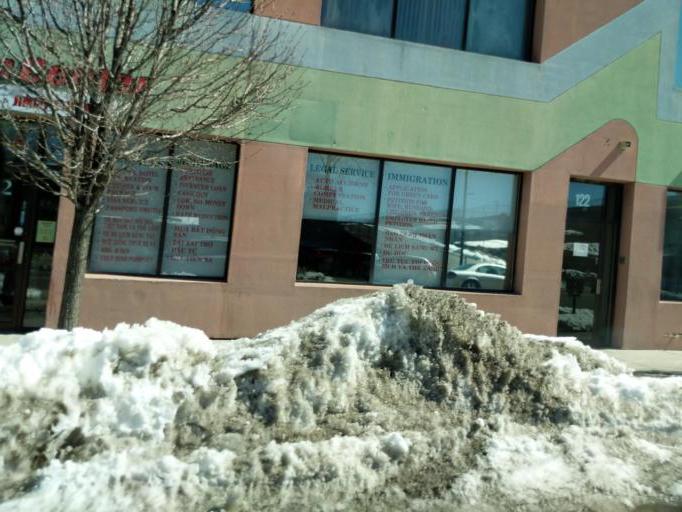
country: US
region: Massachusetts
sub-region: Worcester County
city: Worcester
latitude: 42.2569
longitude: -71.7979
